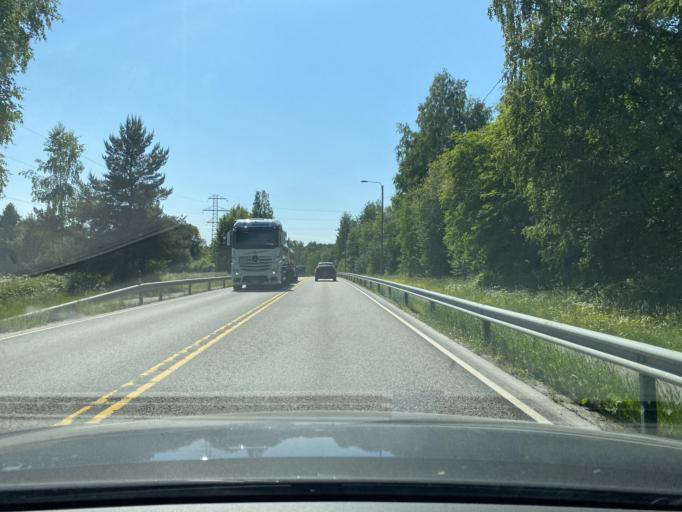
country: FI
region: Pirkanmaa
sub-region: Tampere
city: Nokia
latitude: 61.4746
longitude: 23.5335
